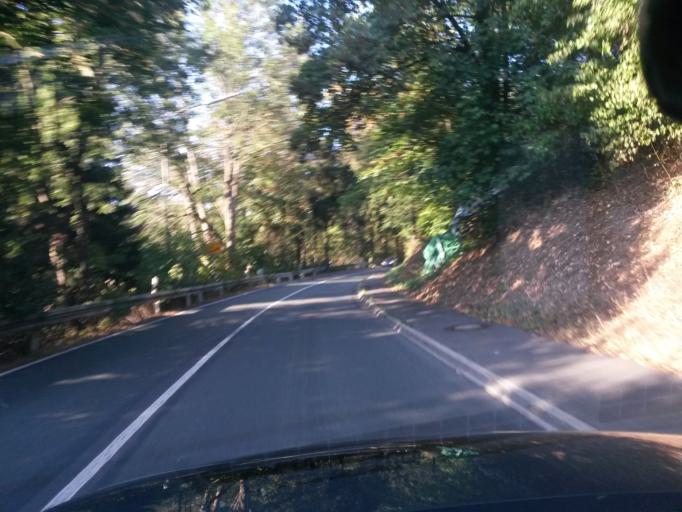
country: DE
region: North Rhine-Westphalia
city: Bergneustadt
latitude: 51.0294
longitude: 7.6171
